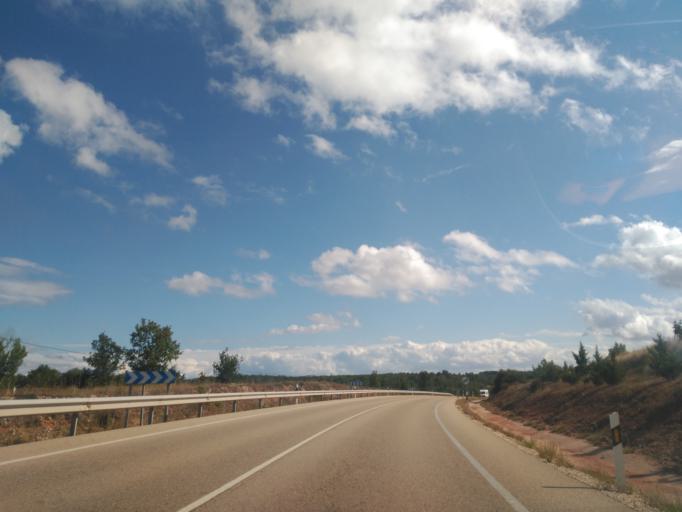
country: ES
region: Castille and Leon
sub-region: Provincia de Burgos
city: Hacinas
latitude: 41.9617
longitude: -3.2917
